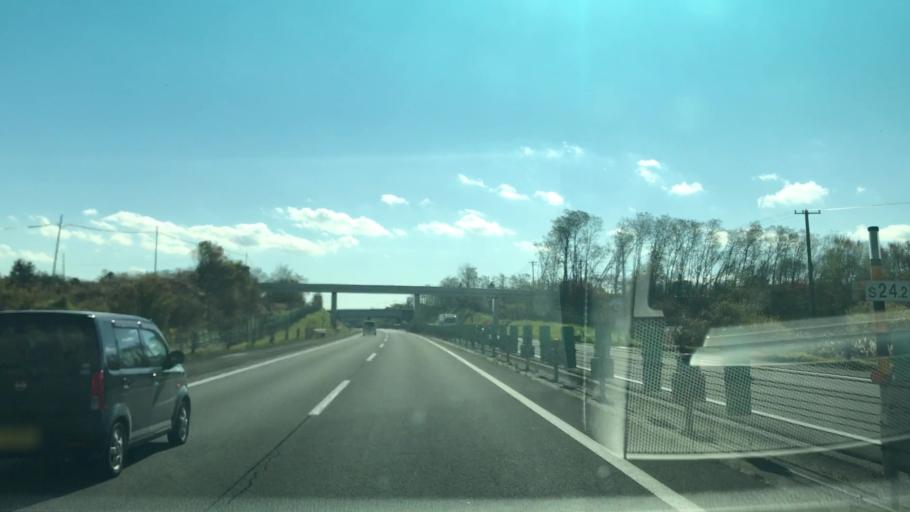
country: JP
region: Hokkaido
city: Kitahiroshima
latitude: 42.8895
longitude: 141.5492
